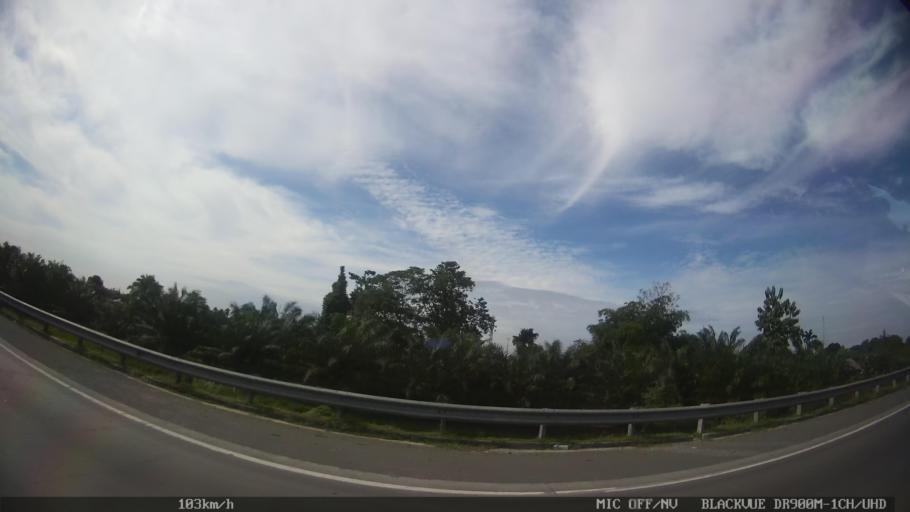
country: ID
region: North Sumatra
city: Sunggal
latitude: 3.6377
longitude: 98.5968
